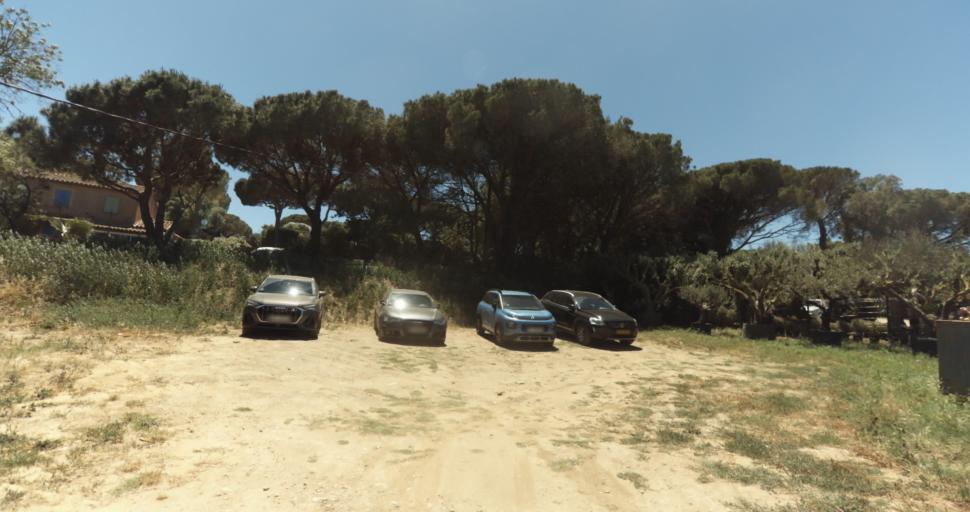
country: FR
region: Provence-Alpes-Cote d'Azur
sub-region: Departement du Var
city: Gassin
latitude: 43.2602
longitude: 6.5722
